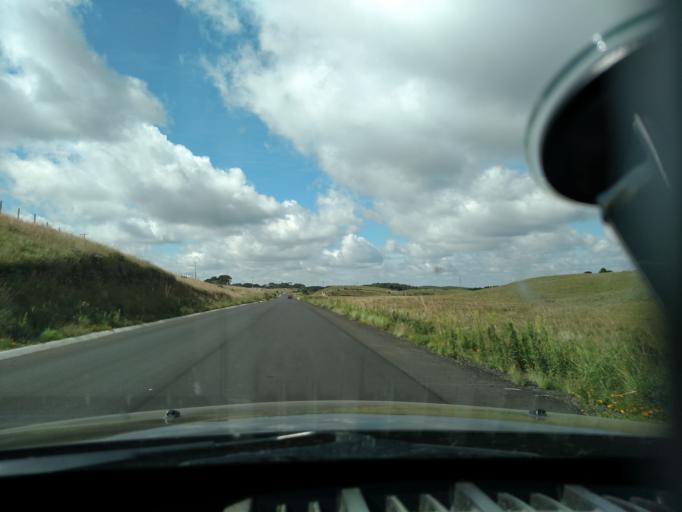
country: BR
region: Santa Catarina
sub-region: Lages
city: Lages
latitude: -28.0114
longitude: -50.0854
